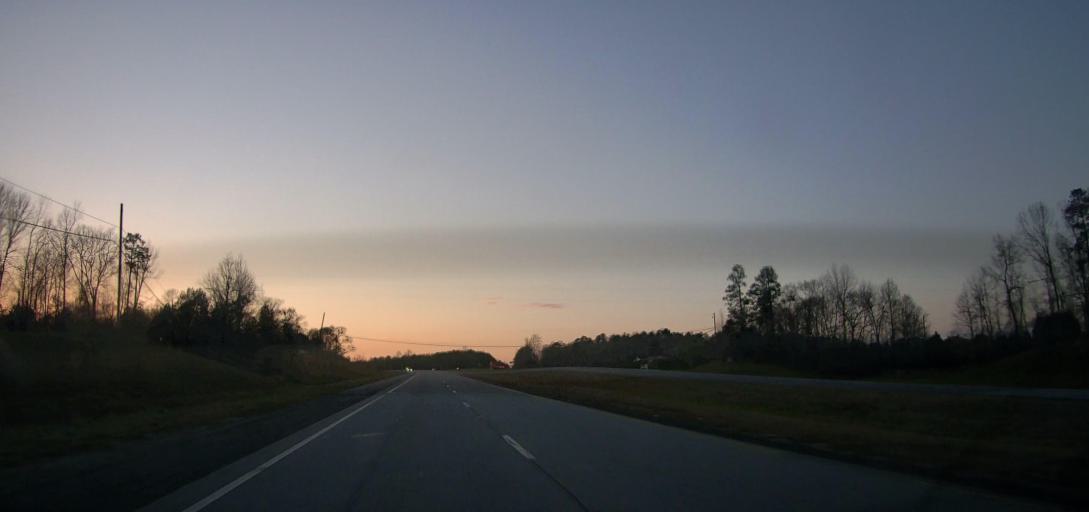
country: US
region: Alabama
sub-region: Tallapoosa County
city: Dadeville
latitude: 32.8766
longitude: -85.8148
